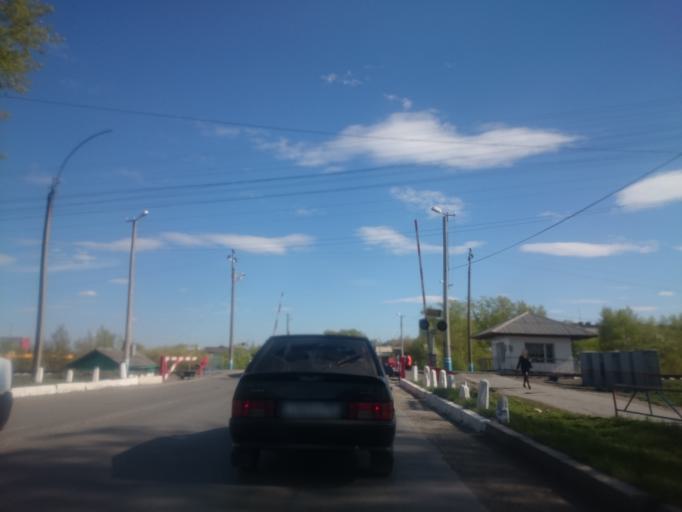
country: RU
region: Sverdlovsk
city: Irbit
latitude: 57.6695
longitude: 63.0747
